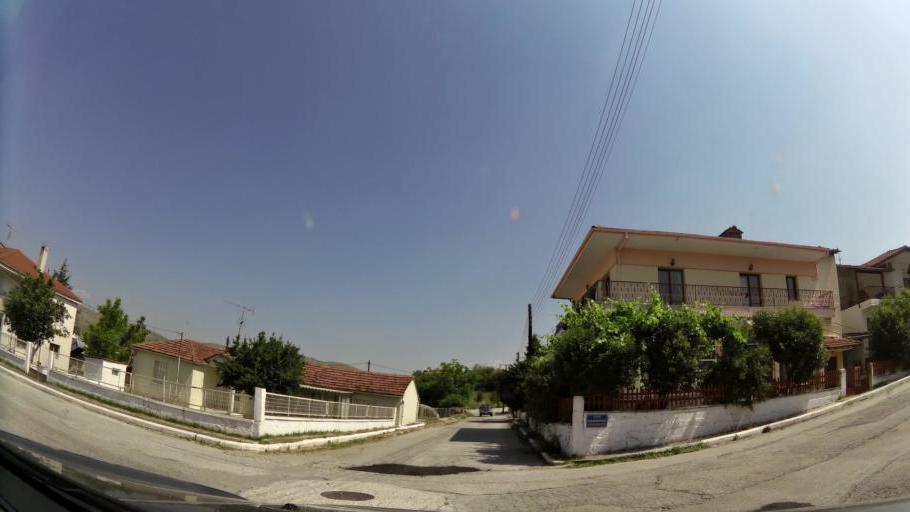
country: GR
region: West Macedonia
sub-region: Nomos Kozanis
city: Koila
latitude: 40.3289
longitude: 21.7935
